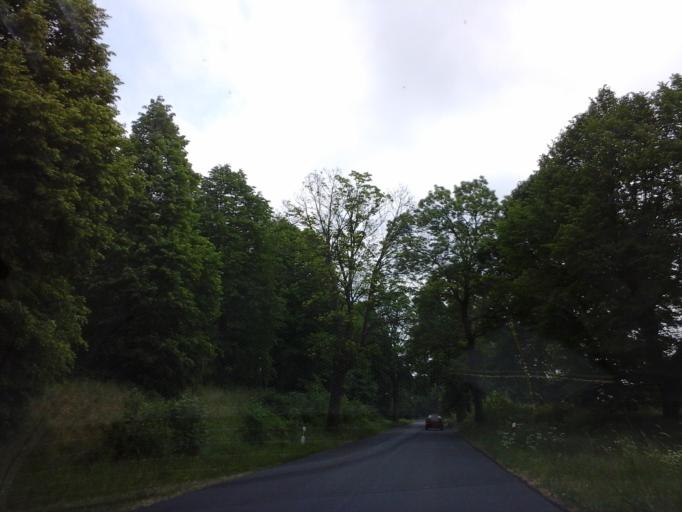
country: PL
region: West Pomeranian Voivodeship
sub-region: Powiat choszczenski
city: Recz
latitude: 53.1898
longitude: 15.6329
